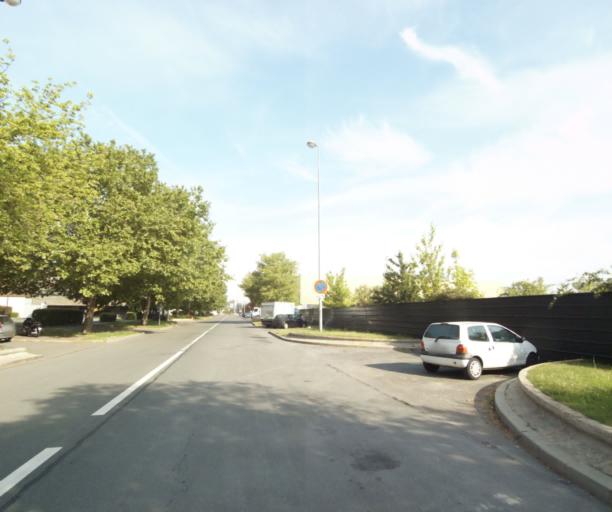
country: FR
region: Ile-de-France
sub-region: Departement des Hauts-de-Seine
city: Bois-Colombes
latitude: 48.9419
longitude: 2.2764
